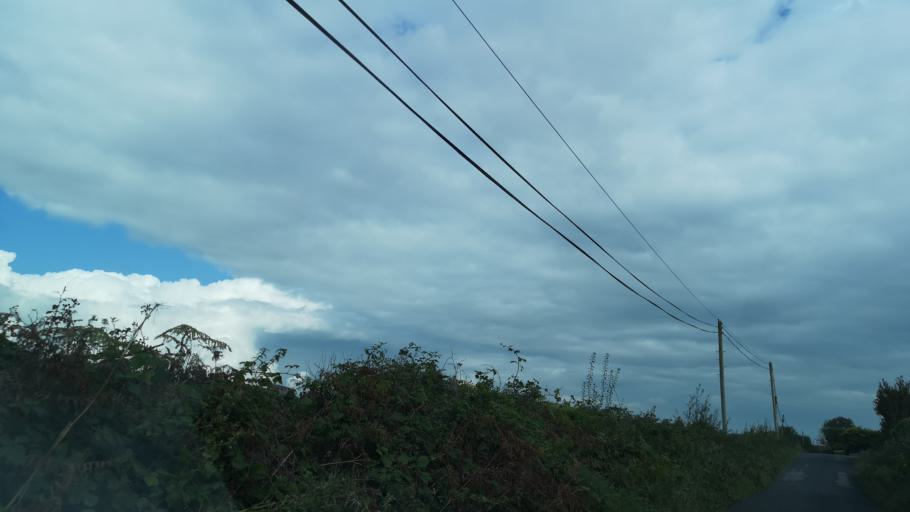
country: IE
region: Connaught
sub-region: County Galway
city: Athenry
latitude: 53.2404
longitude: -8.7345
